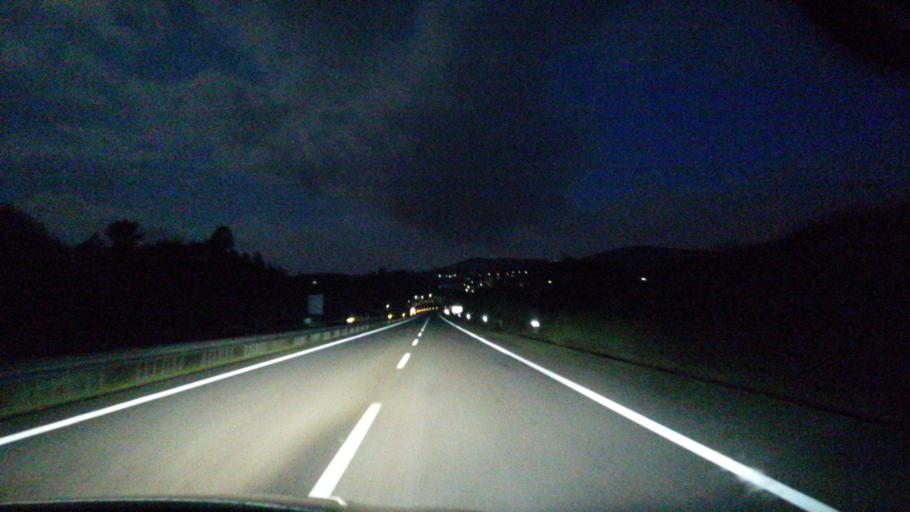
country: PT
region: Porto
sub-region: Lousada
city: Meinedo
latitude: 41.2705
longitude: -8.2344
